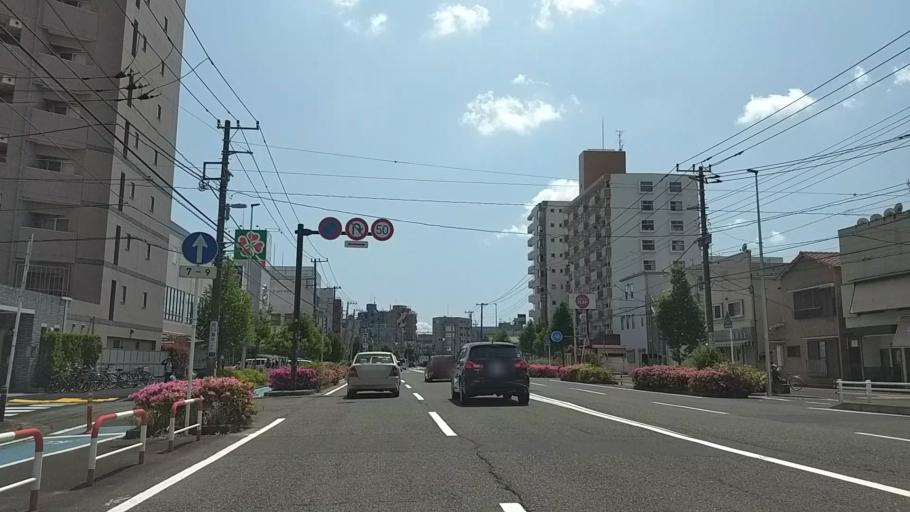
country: JP
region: Kanagawa
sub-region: Kawasaki-shi
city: Kawasaki
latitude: 35.5248
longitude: 139.7134
